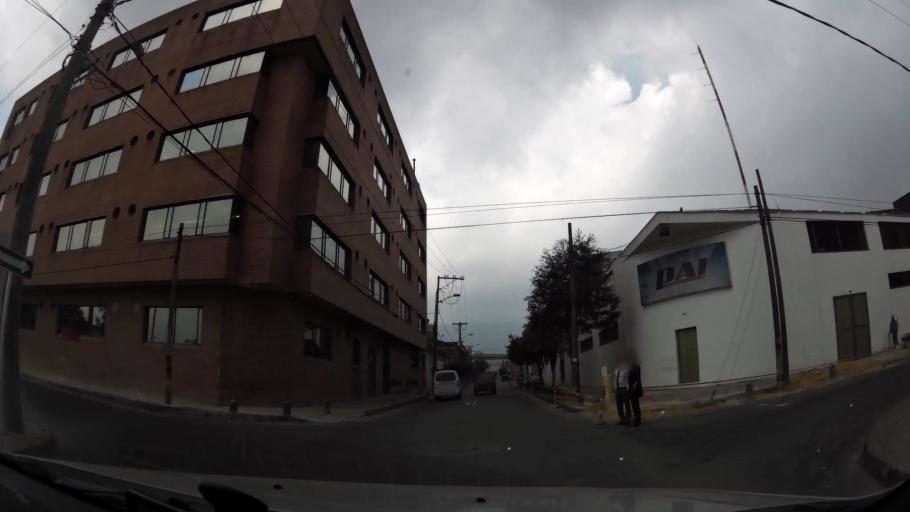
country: CO
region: Bogota D.C.
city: Bogota
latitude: 4.6198
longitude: -74.0930
